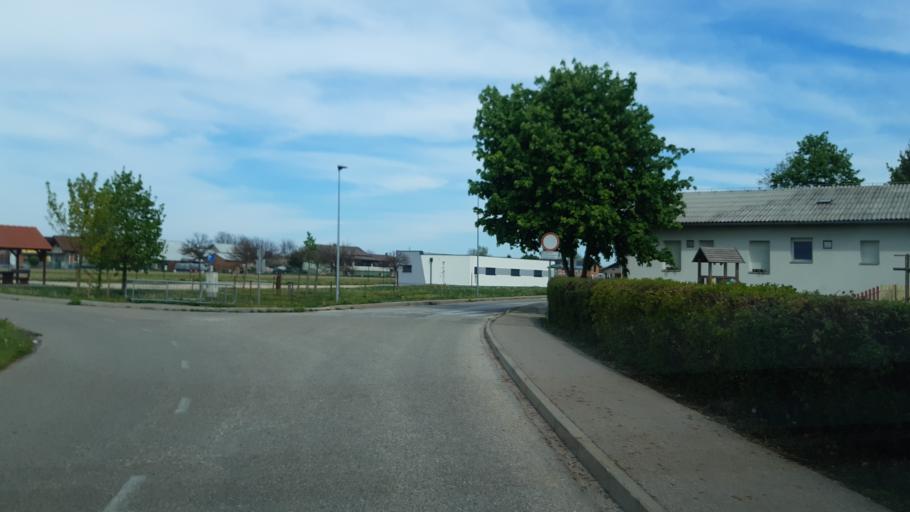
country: SI
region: Murska Sobota
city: Krog
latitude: 46.6533
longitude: 16.1414
